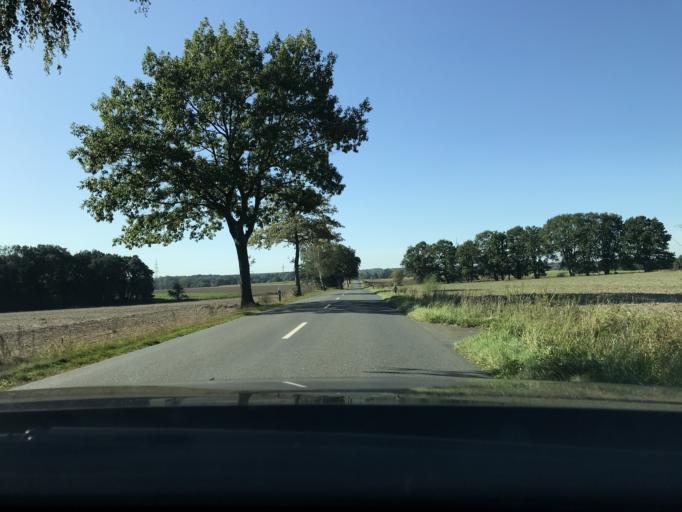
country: DE
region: Lower Saxony
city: Gerdau
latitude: 52.9759
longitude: 10.4315
